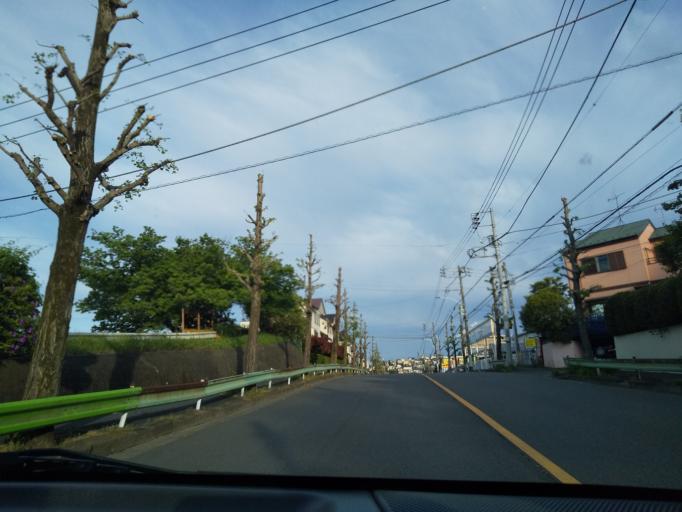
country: JP
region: Tokyo
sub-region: Machida-shi
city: Machida
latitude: 35.5718
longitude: 139.4470
